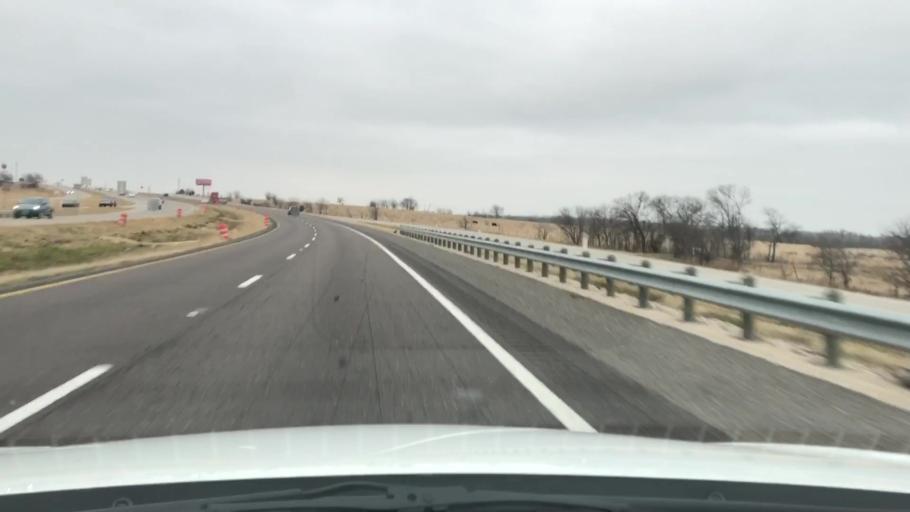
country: US
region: Texas
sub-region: Cooke County
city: Gainesville
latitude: 33.6708
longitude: -97.1508
